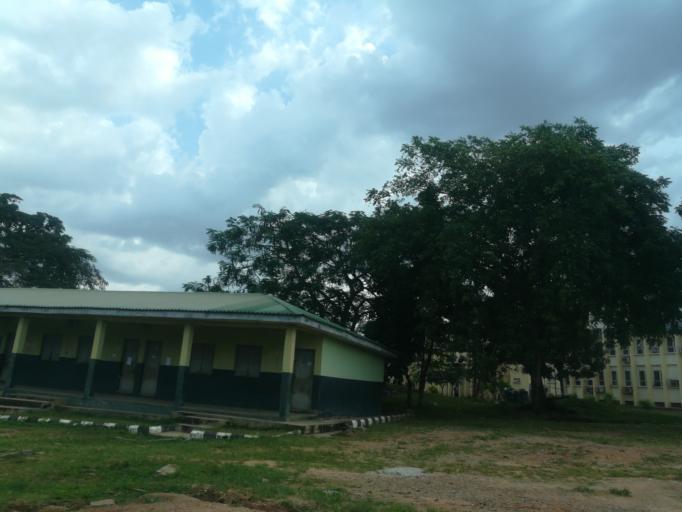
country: NG
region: Oyo
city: Ibadan
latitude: 7.4507
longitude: 3.9045
